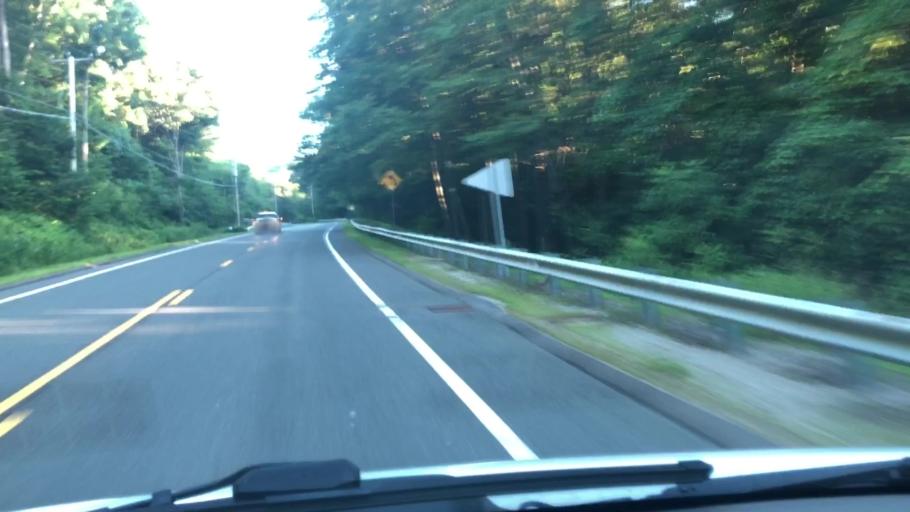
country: US
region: Massachusetts
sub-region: Hampshire County
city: Westhampton
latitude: 42.2838
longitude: -72.7952
